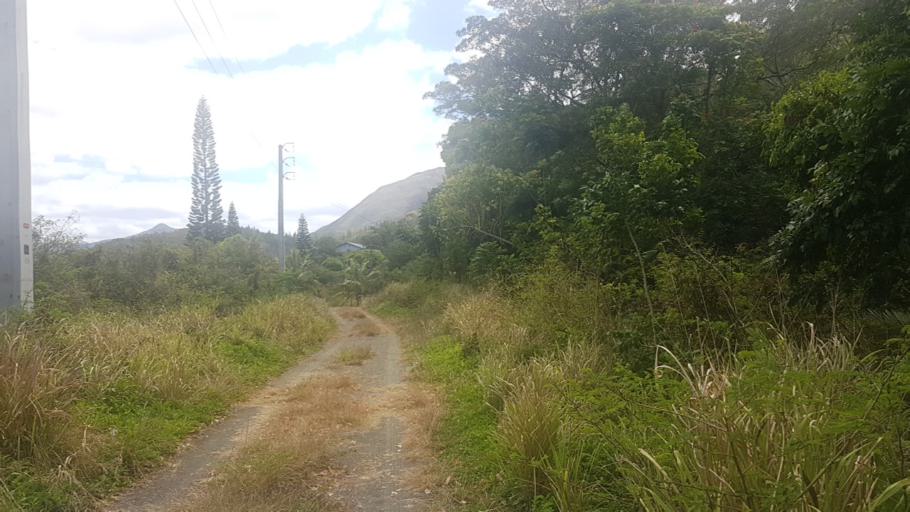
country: NC
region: South Province
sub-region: Dumbea
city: Dumbea
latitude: -22.1848
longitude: 166.4793
